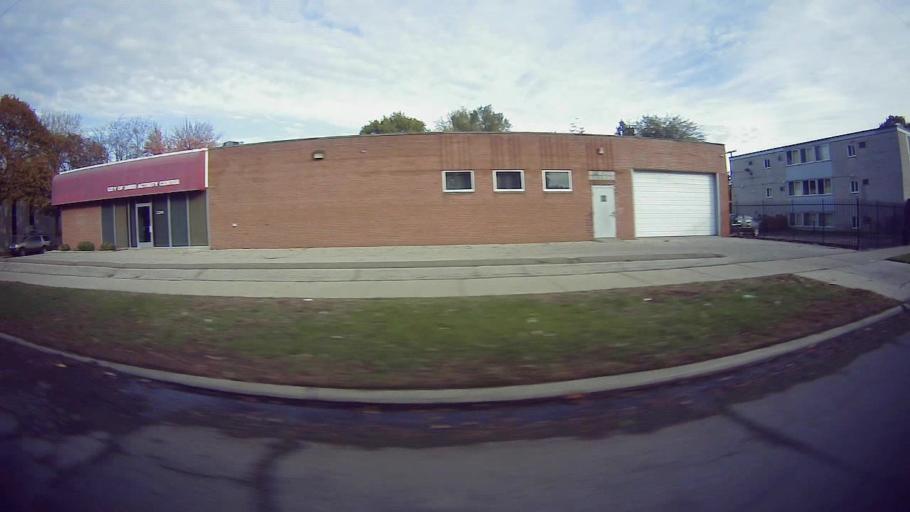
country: US
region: Michigan
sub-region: Wayne County
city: Redford
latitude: 42.4292
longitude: -83.2627
